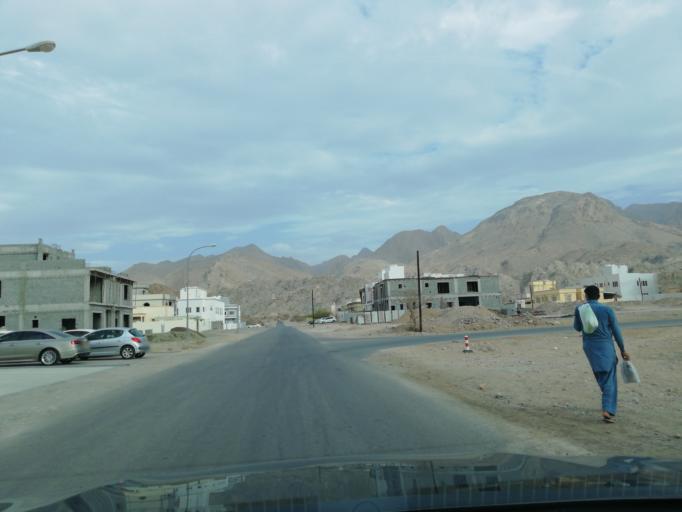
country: OM
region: Muhafazat Masqat
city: Bawshar
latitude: 23.4759
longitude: 58.3071
